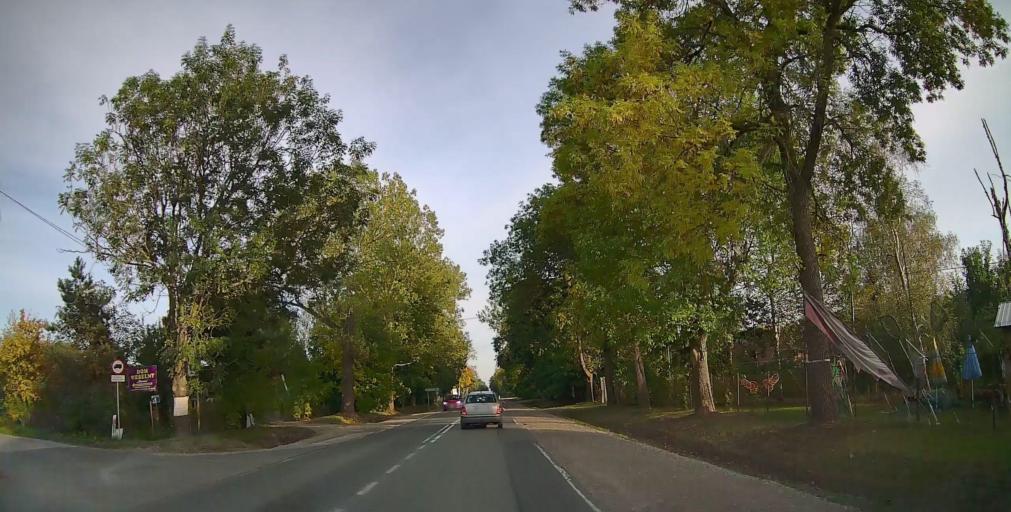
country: PL
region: Masovian Voivodeship
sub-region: Powiat piaseczynski
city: Zabieniec
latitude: 52.0552
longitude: 21.0552
